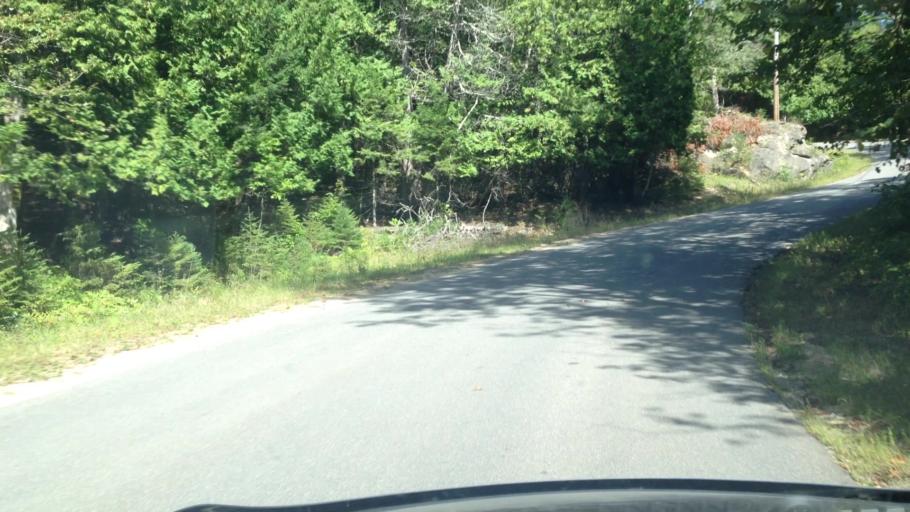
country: CA
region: Quebec
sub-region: Laurentides
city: Mont-Tremblant
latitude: 45.9411
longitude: -74.5873
